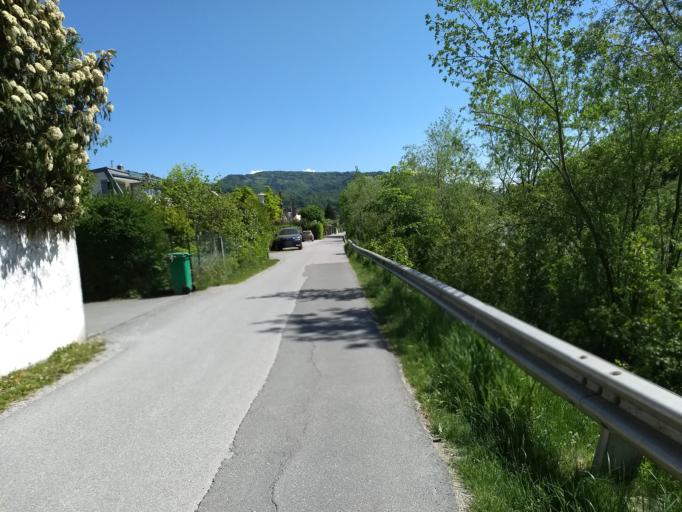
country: AT
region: Salzburg
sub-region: Salzburg Stadt
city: Salzburg
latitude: 47.7871
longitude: 13.0735
